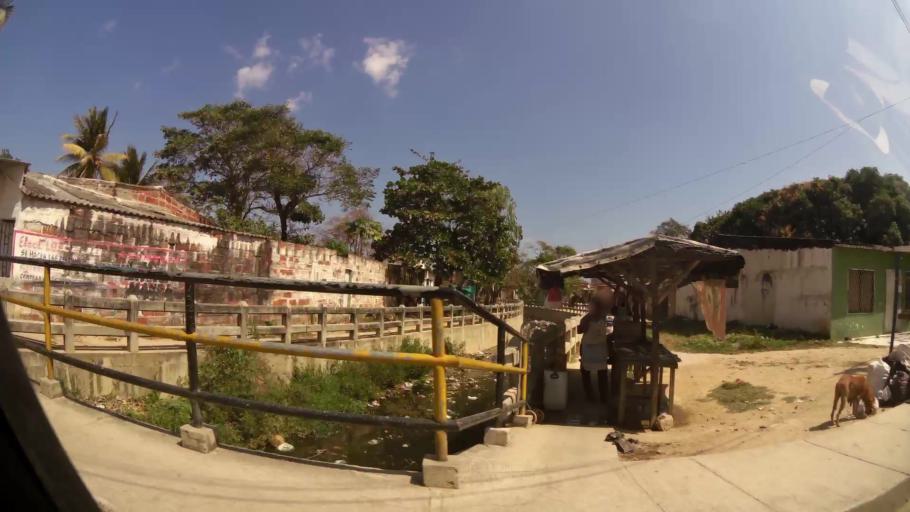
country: CO
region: Atlantico
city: Barranquilla
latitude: 10.9637
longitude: -74.8302
